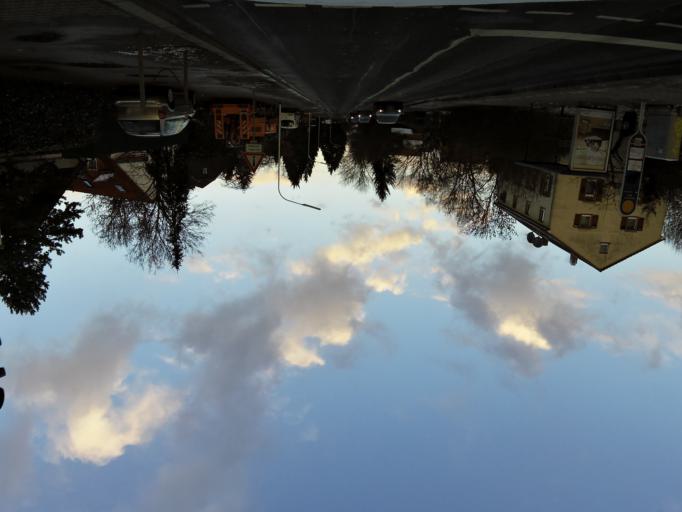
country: DE
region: Hesse
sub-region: Regierungsbezirk Darmstadt
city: Darmstadt
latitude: 49.8853
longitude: 8.6688
